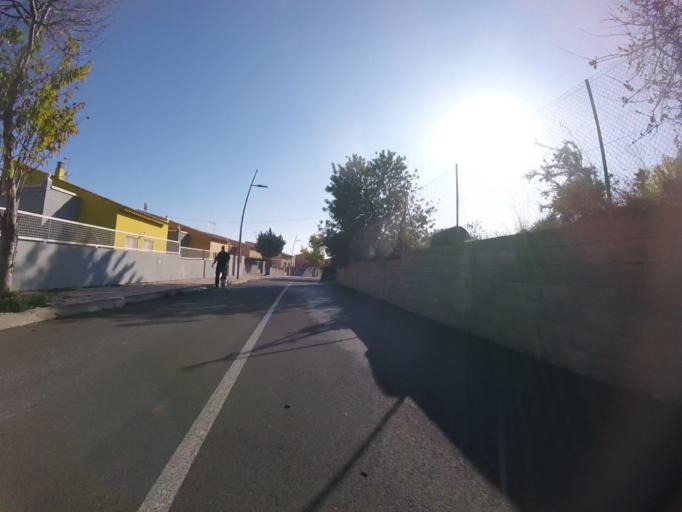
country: ES
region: Valencia
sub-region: Provincia de Castello
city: Peniscola
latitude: 40.3887
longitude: 0.3760
